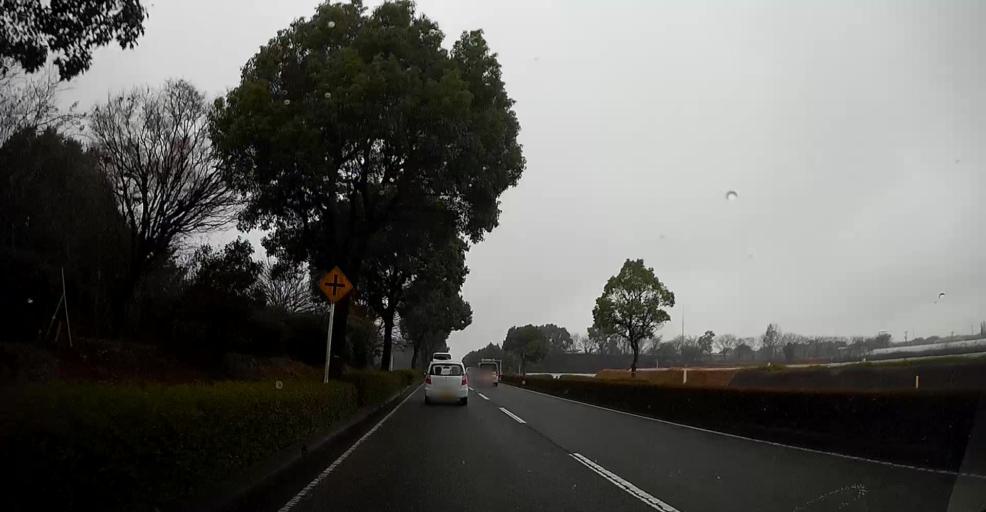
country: JP
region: Kumamoto
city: Ozu
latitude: 32.8216
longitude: 130.8506
